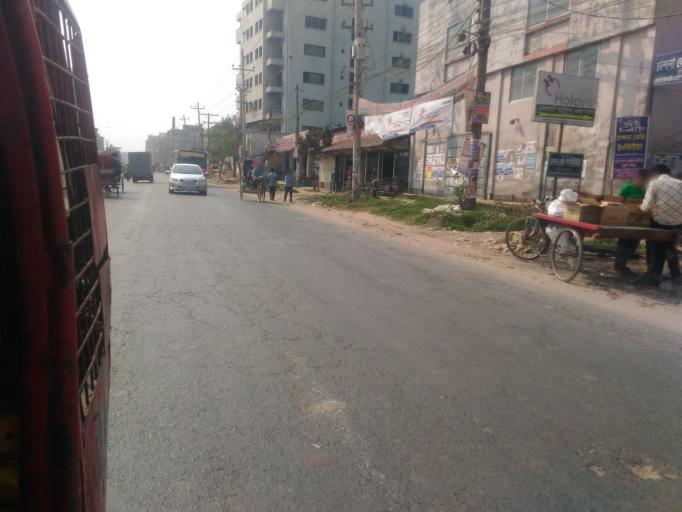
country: BD
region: Dhaka
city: Tungi
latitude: 23.9911
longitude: 90.3910
